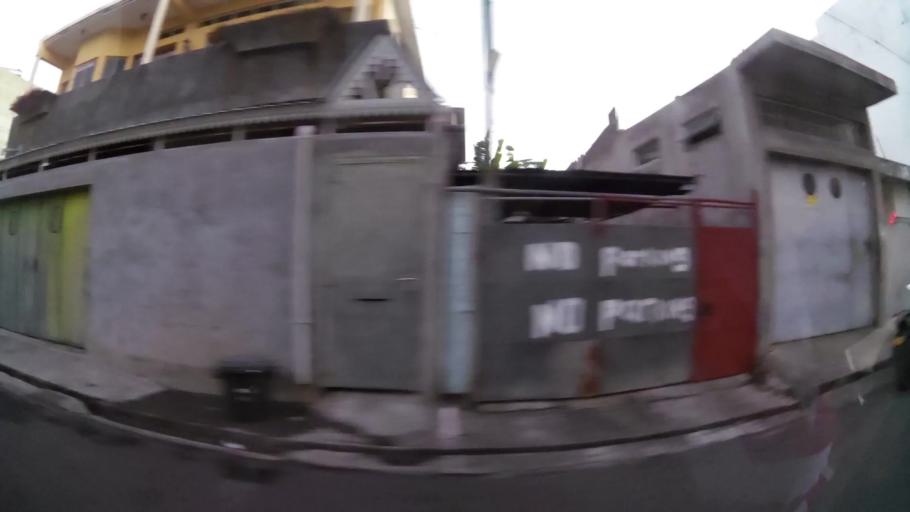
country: MU
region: Port Louis
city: Port Louis
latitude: -20.1659
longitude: 57.5143
